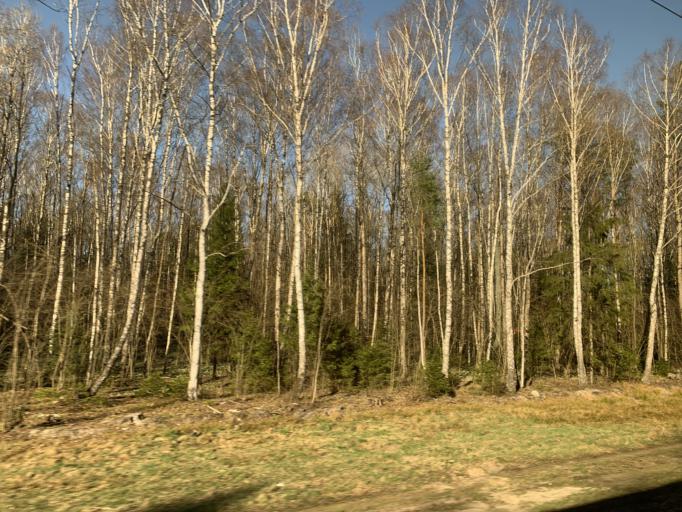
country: BY
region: Grodnenskaya
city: Smarhon'
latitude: 54.4888
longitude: 26.3048
